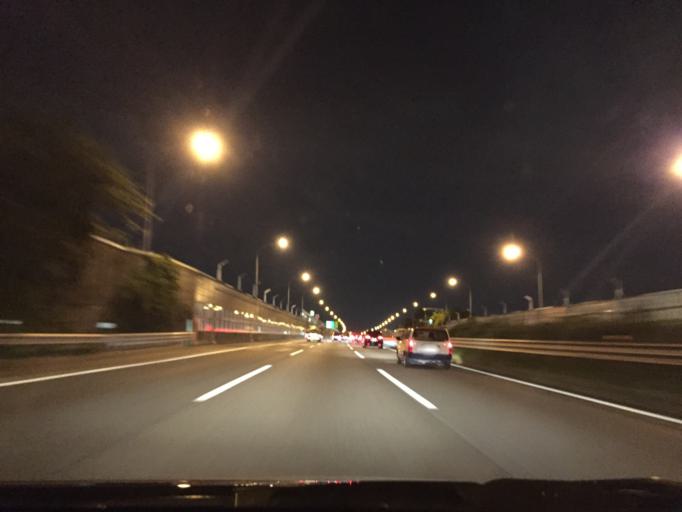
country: JP
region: Kanagawa
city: Minami-rinkan
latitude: 35.4852
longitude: 139.4646
